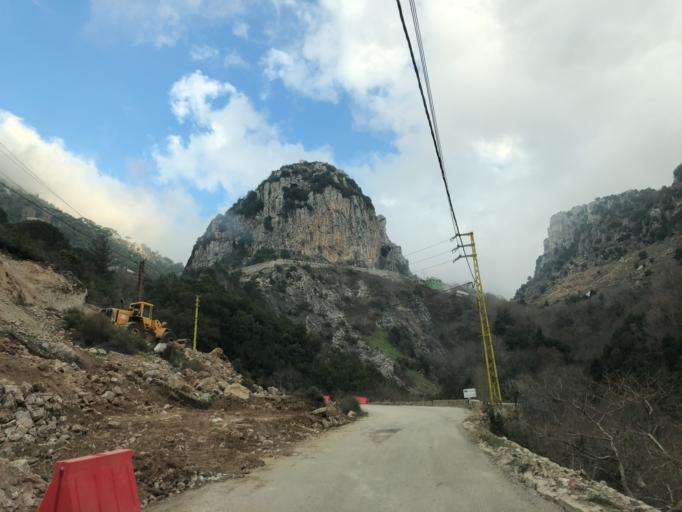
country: LB
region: Liban-Nord
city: Amioun
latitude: 34.1962
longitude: 35.8892
